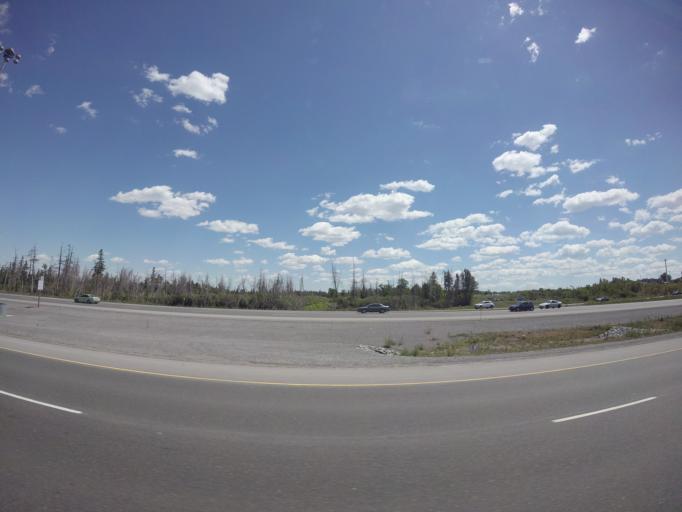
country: CA
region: Ontario
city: Bells Corners
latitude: 45.2834
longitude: -75.9541
